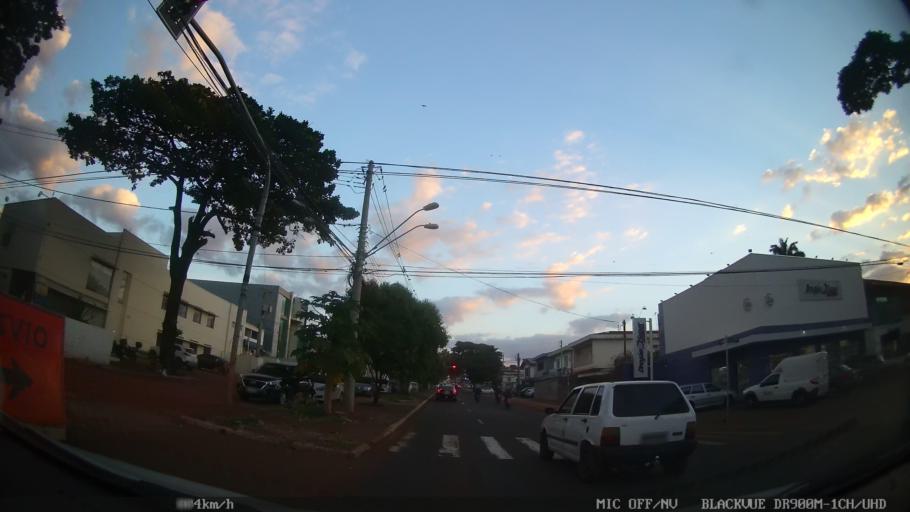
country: BR
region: Sao Paulo
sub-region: Ribeirao Preto
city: Ribeirao Preto
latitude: -21.1881
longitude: -47.8072
